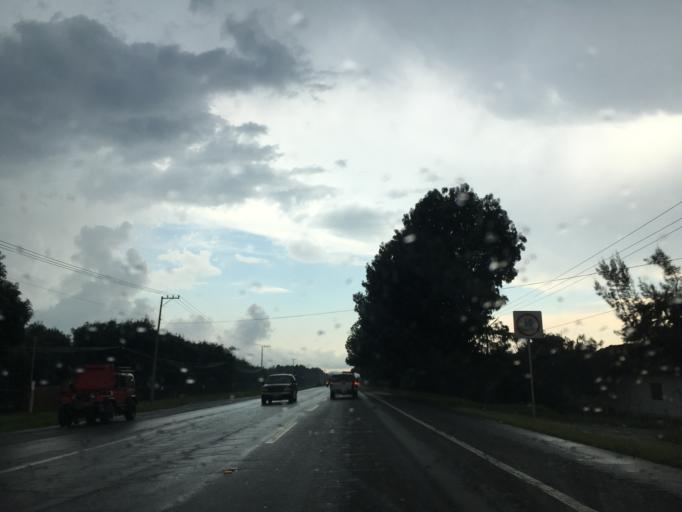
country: MX
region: Michoacan
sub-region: Uruapan
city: Uruapan
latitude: 19.4597
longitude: -102.0760
